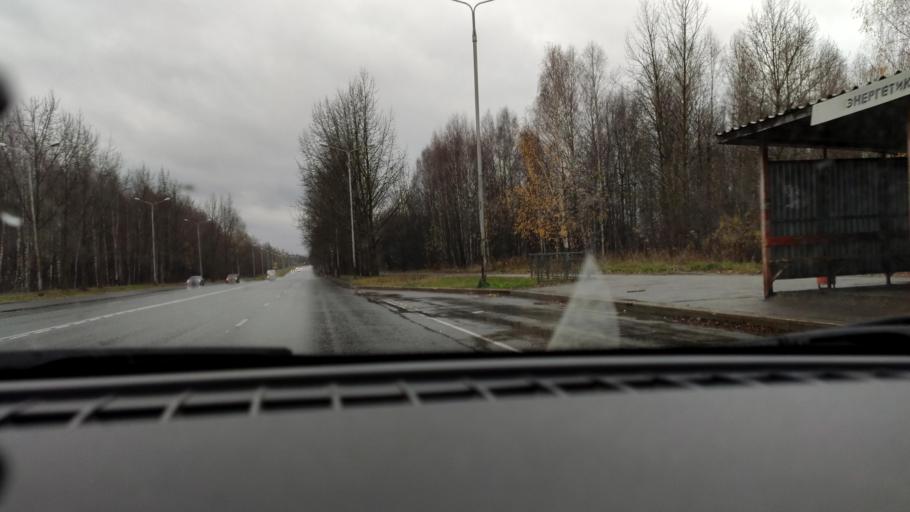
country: RU
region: Perm
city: Perm
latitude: 58.1077
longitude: 56.3961
